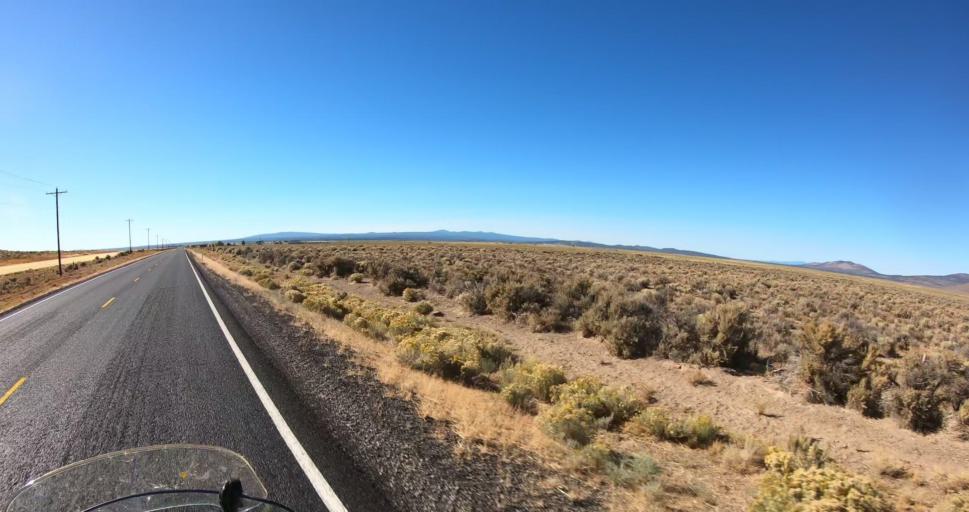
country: US
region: Oregon
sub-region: Deschutes County
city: La Pine
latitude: 43.1287
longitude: -120.9657
